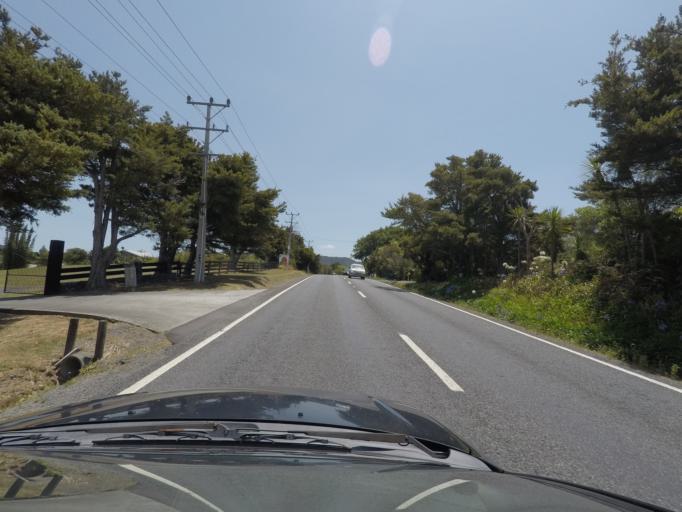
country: NZ
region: Auckland
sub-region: Auckland
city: Warkworth
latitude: -36.3888
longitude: 174.6601
